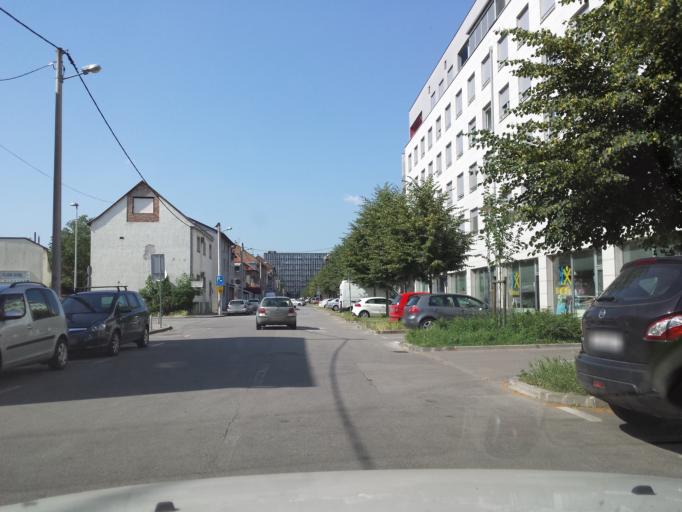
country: HR
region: Grad Zagreb
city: Novi Zagreb
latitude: 45.7959
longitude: 15.9806
